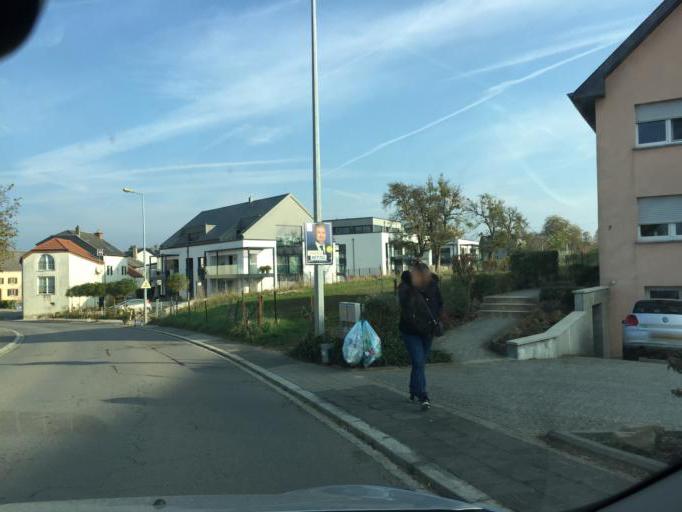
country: LU
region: Luxembourg
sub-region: Canton de Luxembourg
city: Contern
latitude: 49.5826
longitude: 6.2249
